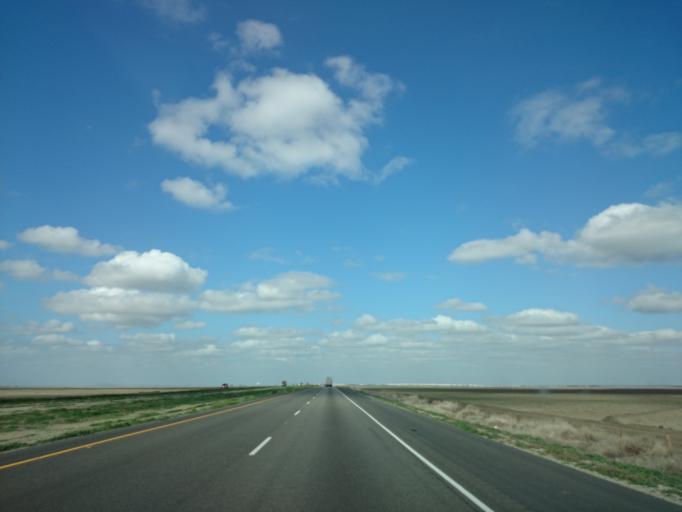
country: US
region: California
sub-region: Kern County
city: Greenfield
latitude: 35.1314
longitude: -119.0771
